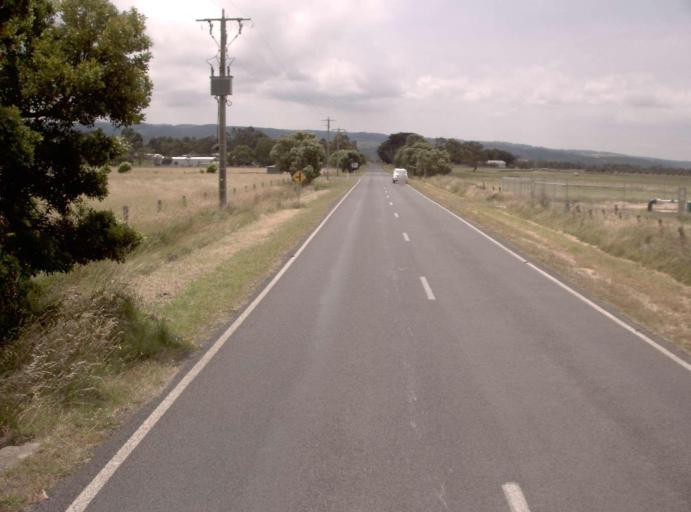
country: AU
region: Victoria
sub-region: Latrobe
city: Traralgon
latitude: -38.5259
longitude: 146.6597
